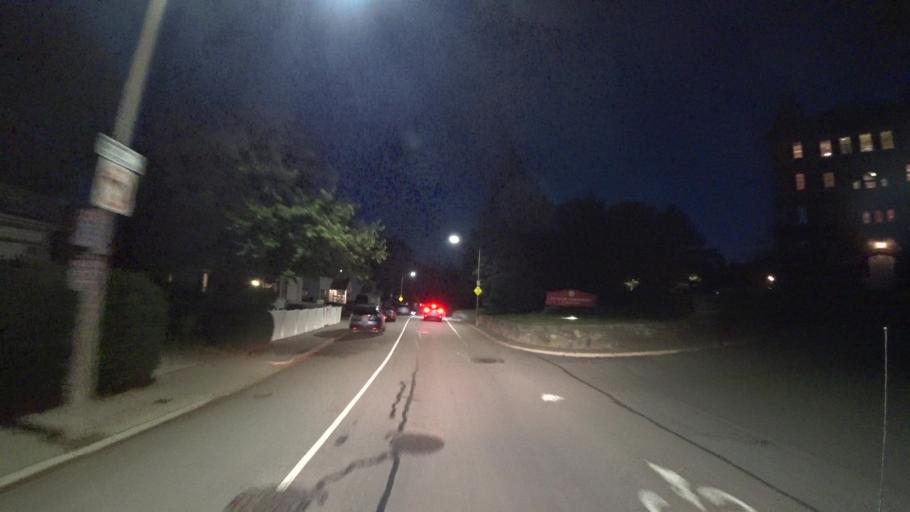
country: US
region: Massachusetts
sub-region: Middlesex County
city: Watertown
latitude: 42.3441
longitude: -71.1641
